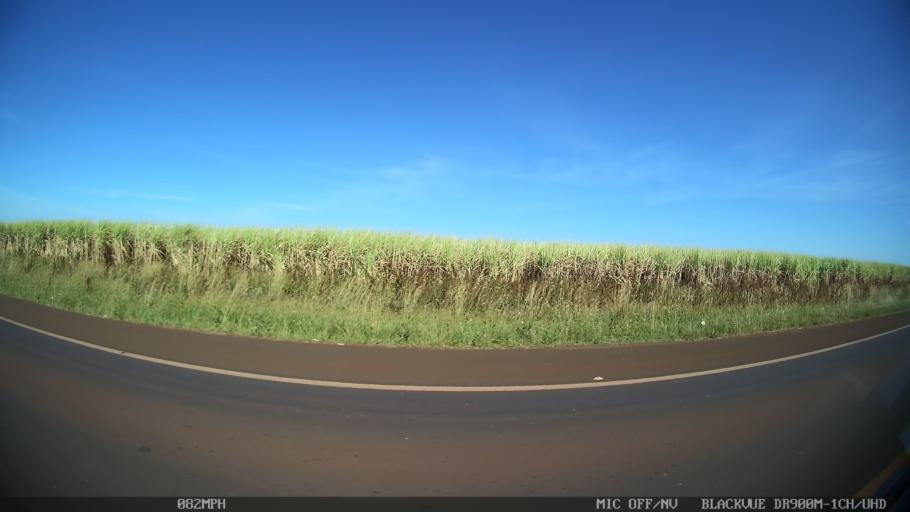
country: BR
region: Sao Paulo
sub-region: Guaira
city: Guaira
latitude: -20.4439
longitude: -48.3486
